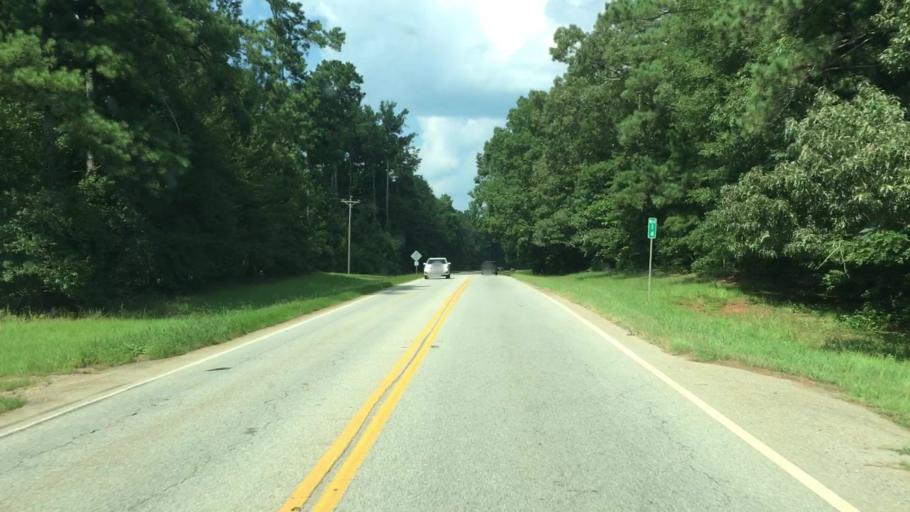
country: US
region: Georgia
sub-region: Monroe County
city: Forsyth
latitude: 33.0534
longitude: -83.9291
